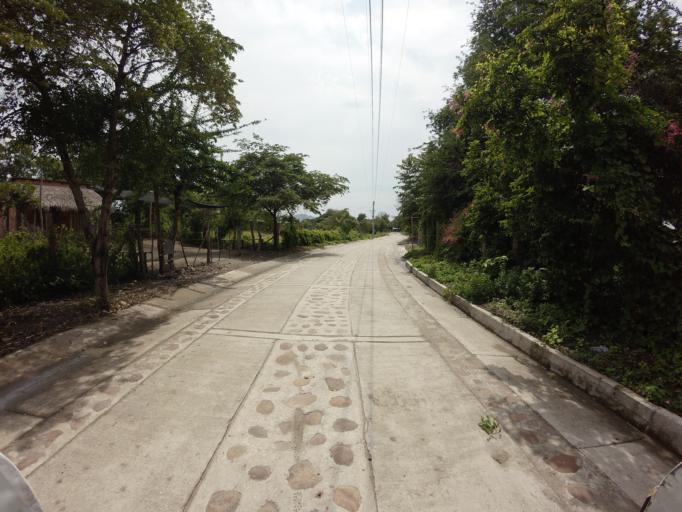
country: CO
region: Tolima
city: Natagaima
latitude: 3.4564
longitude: -75.1436
